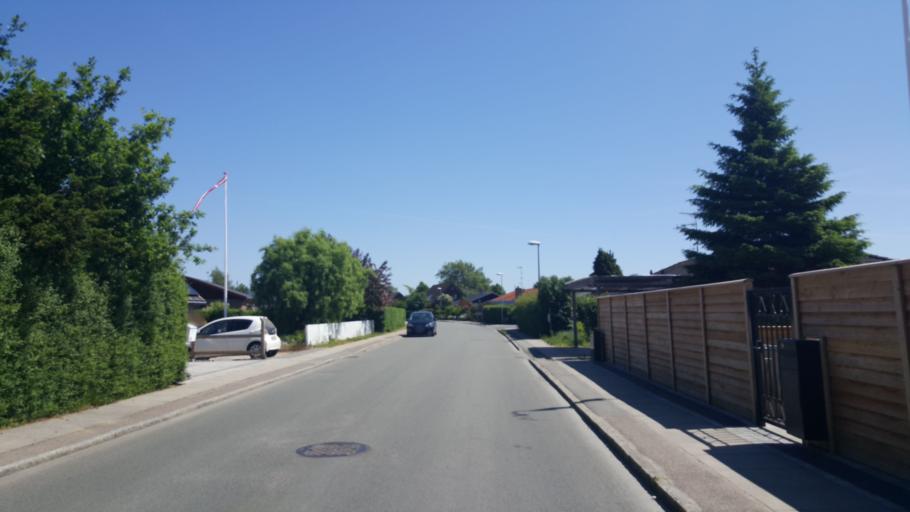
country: DK
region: Capital Region
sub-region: Tarnby Kommune
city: Tarnby
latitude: 55.6173
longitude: 12.5947
